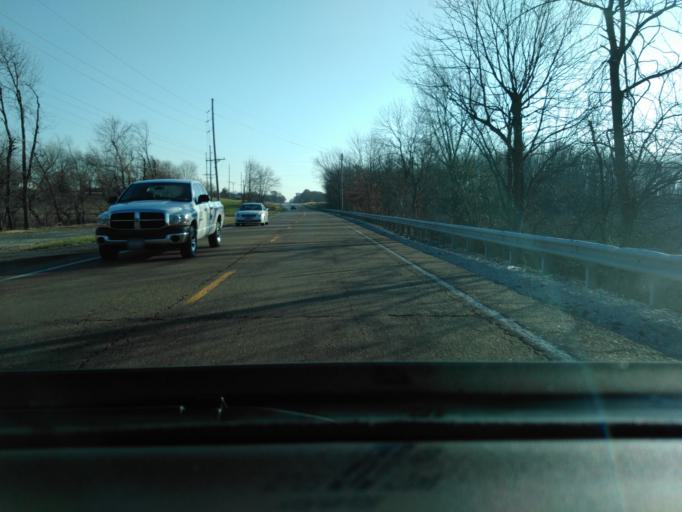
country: US
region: Illinois
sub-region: Madison County
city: Saint Jacob
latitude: 38.7162
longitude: -89.8255
